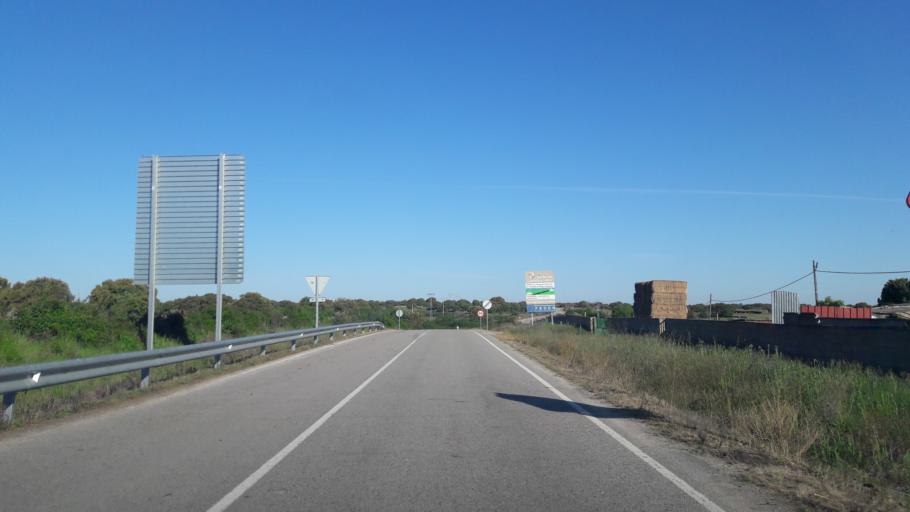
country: ES
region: Castille and Leon
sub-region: Provincia de Salamanca
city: Villavieja de Yeltes
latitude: 40.8776
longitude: -6.4723
